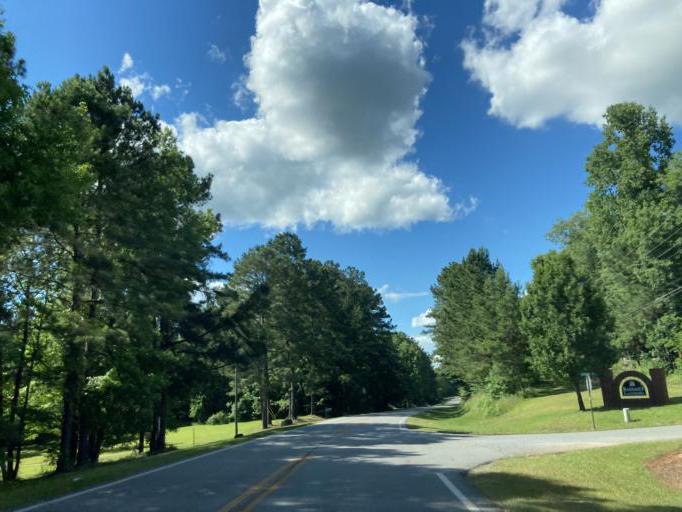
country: US
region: Georgia
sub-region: Jones County
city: Gray
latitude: 32.9847
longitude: -83.5504
